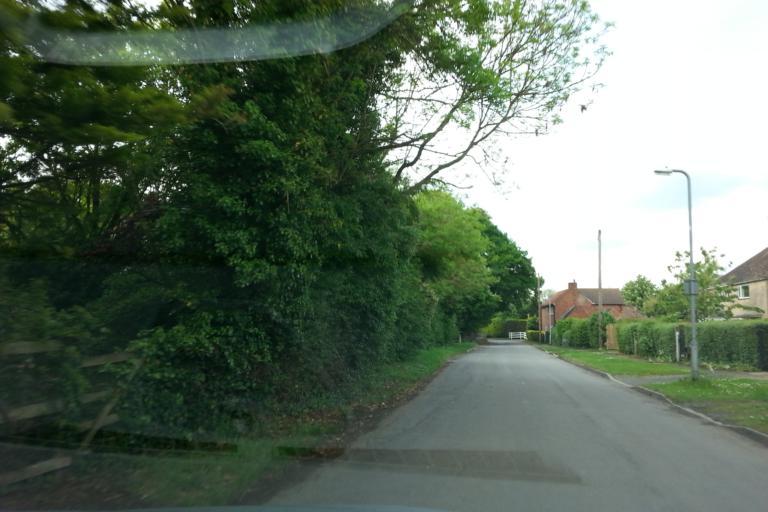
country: GB
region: England
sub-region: Lincolnshire
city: Long Bennington
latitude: 53.0110
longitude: -0.7335
